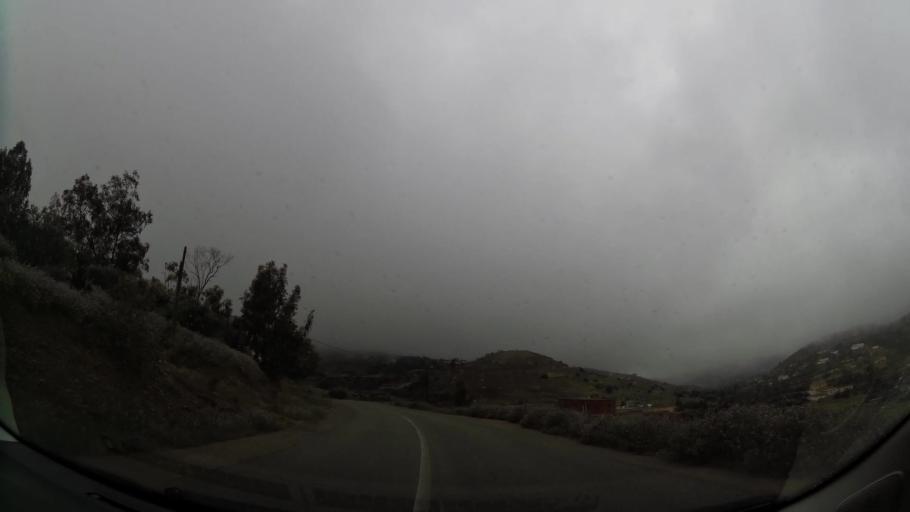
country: MA
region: Oriental
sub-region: Nador
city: Boudinar
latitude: 35.0897
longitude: -3.5200
